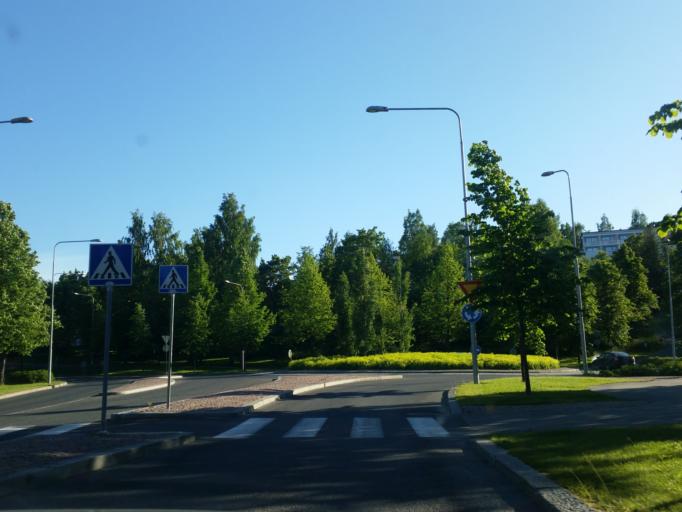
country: FI
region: Northern Savo
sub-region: Kuopio
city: Kuopio
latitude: 62.8868
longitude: 27.6794
